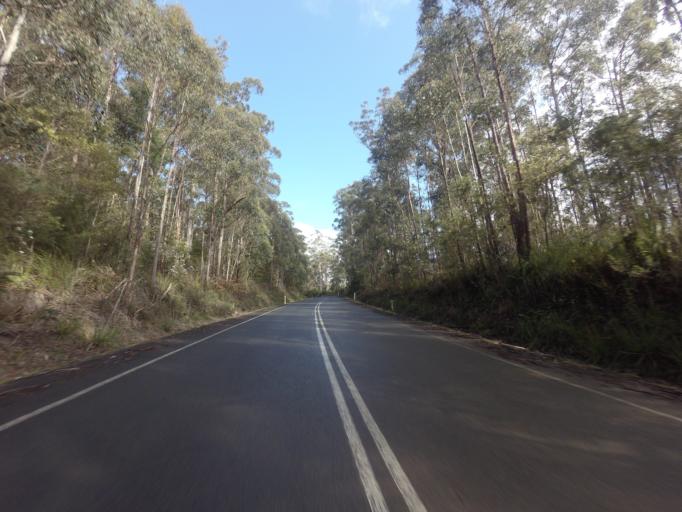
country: AU
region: Tasmania
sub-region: Huon Valley
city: Geeveston
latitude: -43.4137
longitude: 146.9156
